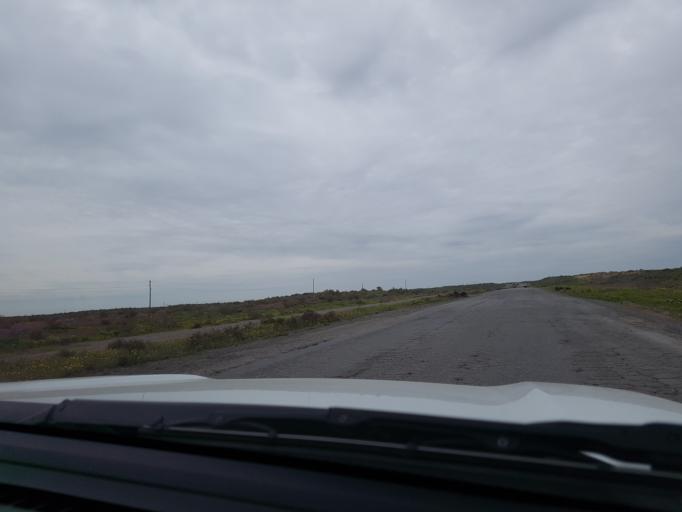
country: TM
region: Mary
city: Bayramaly
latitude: 37.9029
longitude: 62.6188
